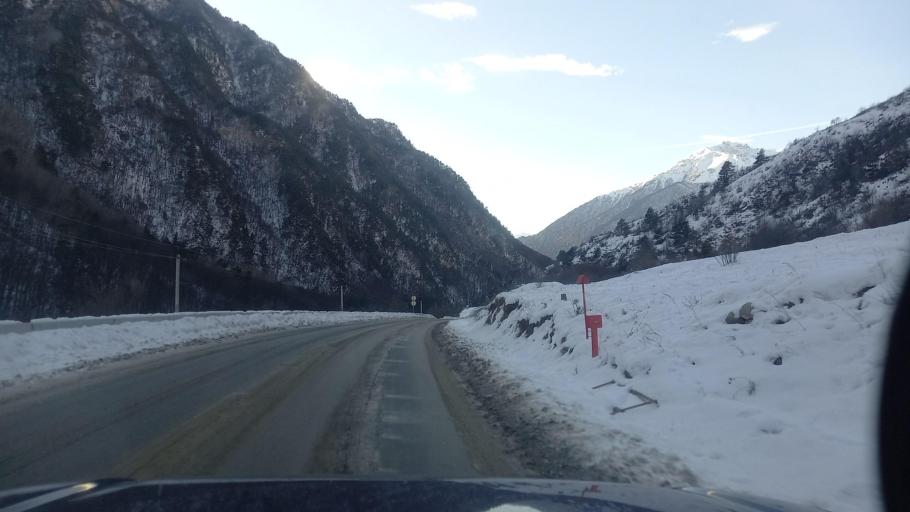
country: RU
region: North Ossetia
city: Chikola
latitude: 42.9773
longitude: 43.7646
